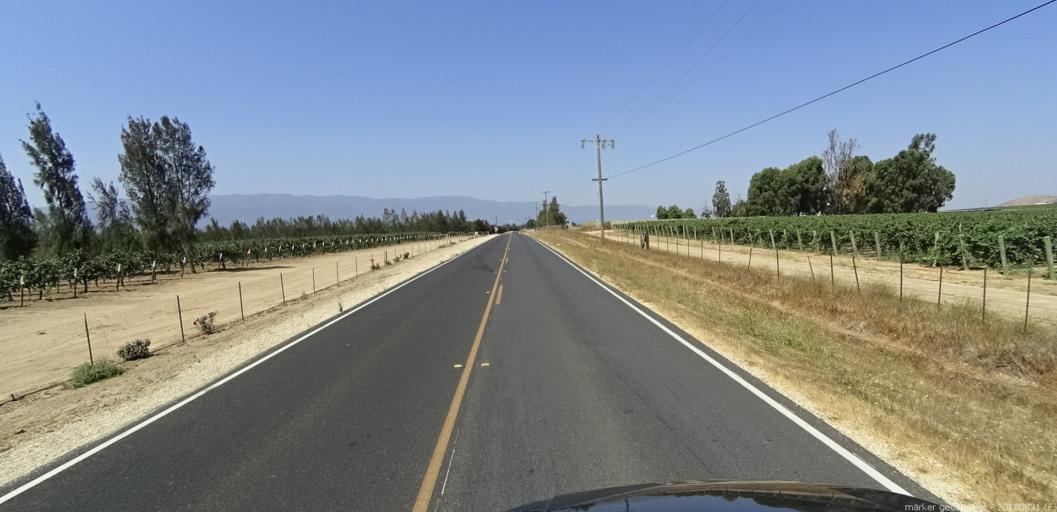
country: US
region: California
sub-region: Monterey County
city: Soledad
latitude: 36.4232
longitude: -121.2880
